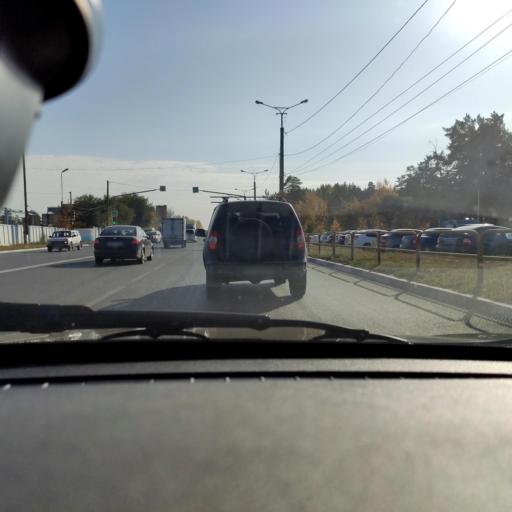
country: RU
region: Samara
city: Zhigulevsk
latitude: 53.4969
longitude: 49.4731
